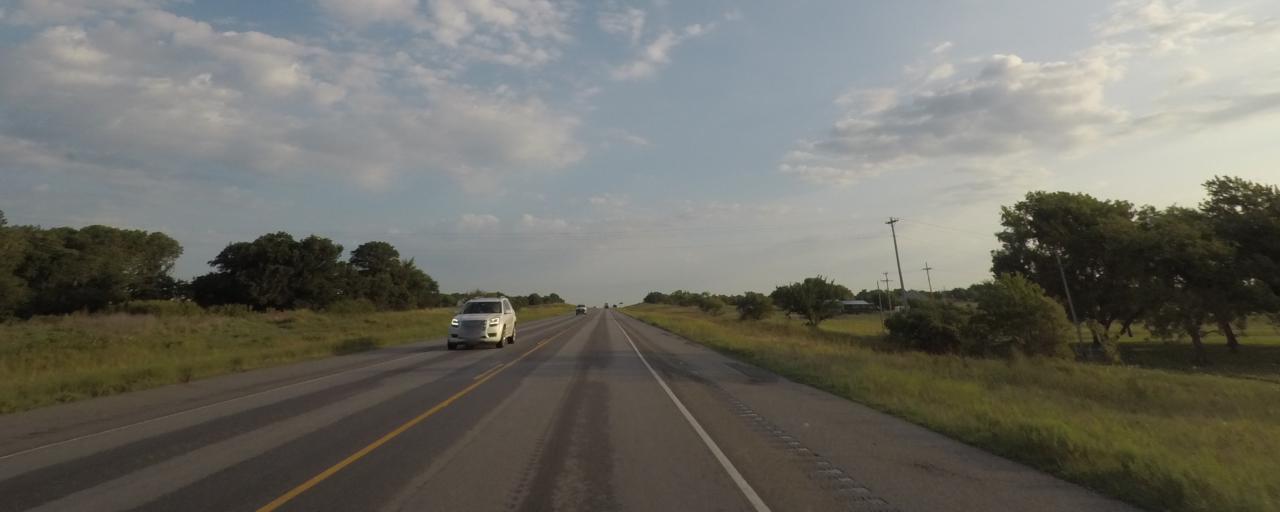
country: US
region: Oklahoma
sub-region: Stephens County
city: Meridian
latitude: 34.4442
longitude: -97.9741
